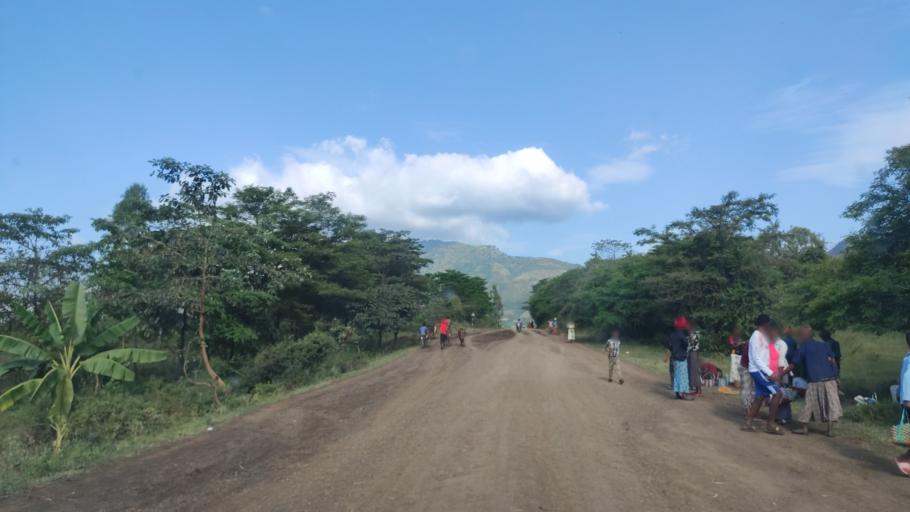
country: ET
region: Southern Nations, Nationalities, and People's Region
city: Felege Neway
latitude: 6.4259
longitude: 37.3161
